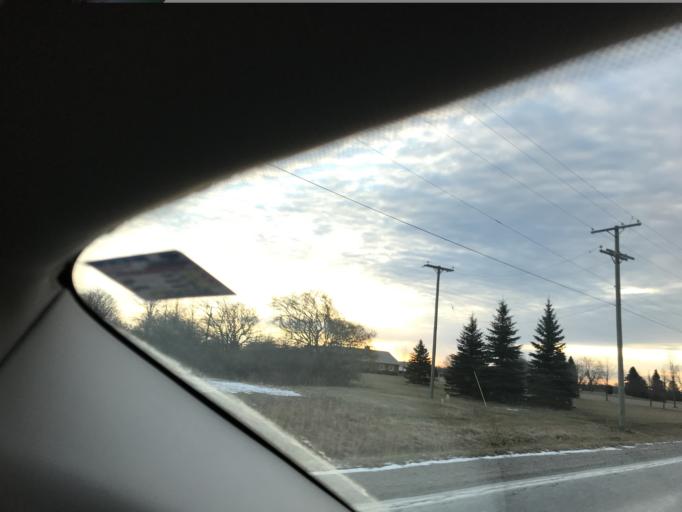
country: US
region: Michigan
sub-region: Macomb County
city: Armada
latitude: 42.8917
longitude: -82.8825
